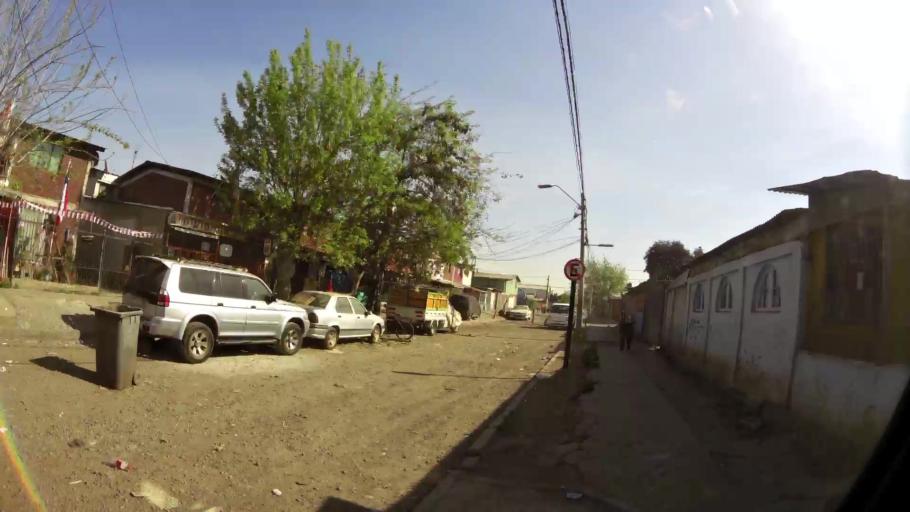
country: CL
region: Santiago Metropolitan
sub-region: Provincia de Santiago
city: Lo Prado
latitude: -33.4188
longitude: -70.7632
